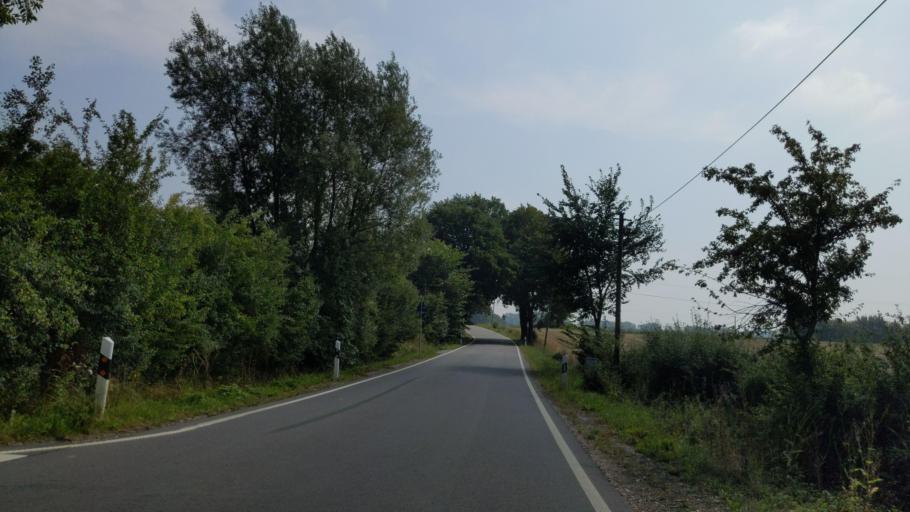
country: DE
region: Schleswig-Holstein
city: Stockelsdorf
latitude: 53.9225
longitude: 10.6155
